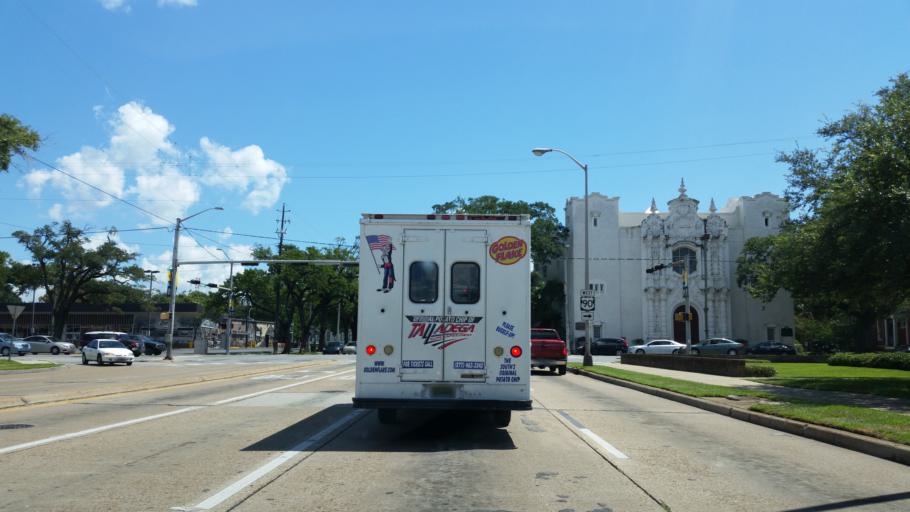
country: US
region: Alabama
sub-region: Mobile County
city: Mobile
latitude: 30.6867
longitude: -88.0540
